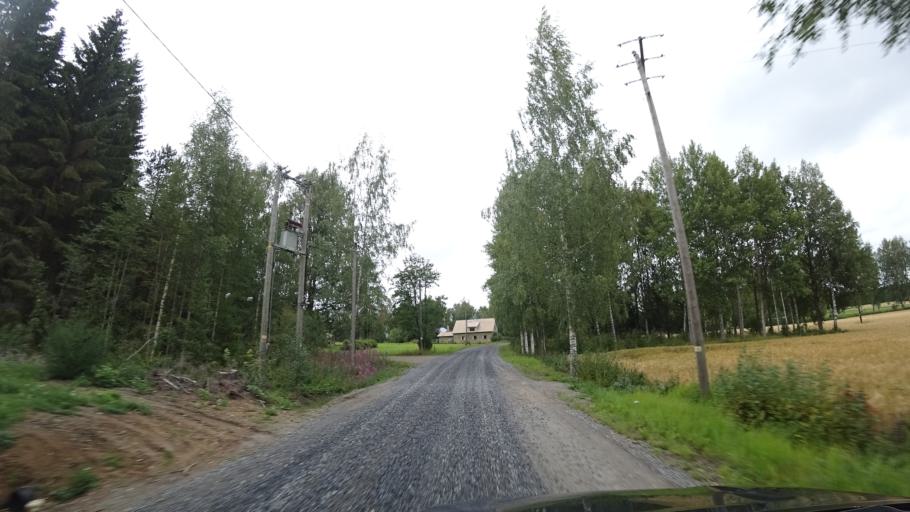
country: FI
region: Haeme
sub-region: Haemeenlinna
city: Lammi
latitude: 61.1262
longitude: 24.9834
